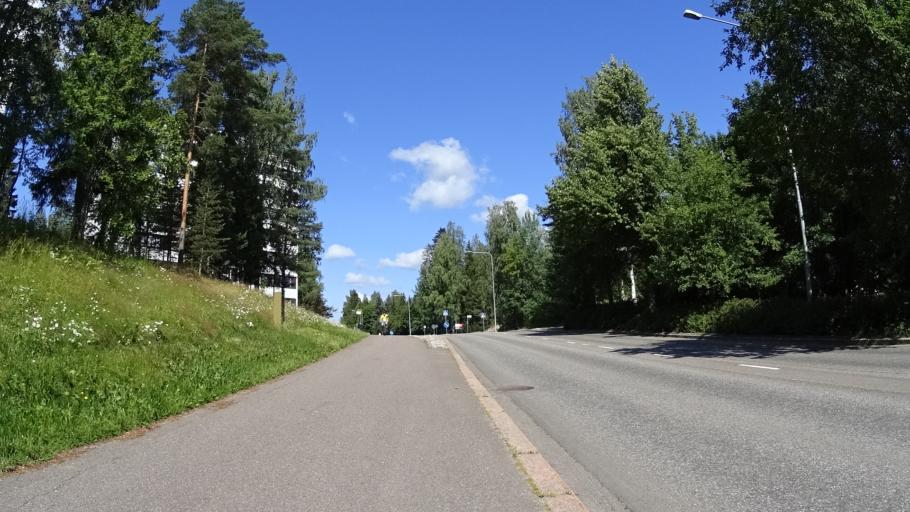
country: FI
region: Uusimaa
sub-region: Helsinki
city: Jaervenpaeae
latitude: 60.4838
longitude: 25.0757
